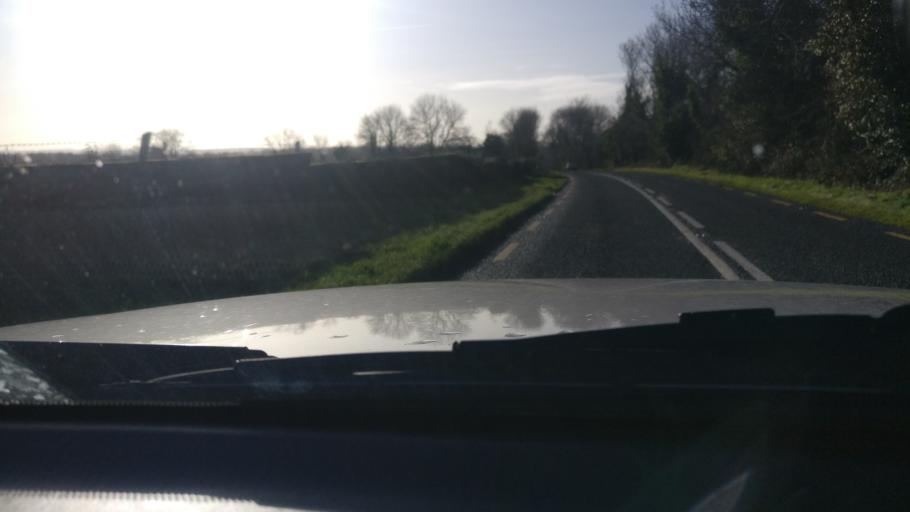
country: IE
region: Leinster
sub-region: An Iarmhi
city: Moate
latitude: 53.6127
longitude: -7.7070
